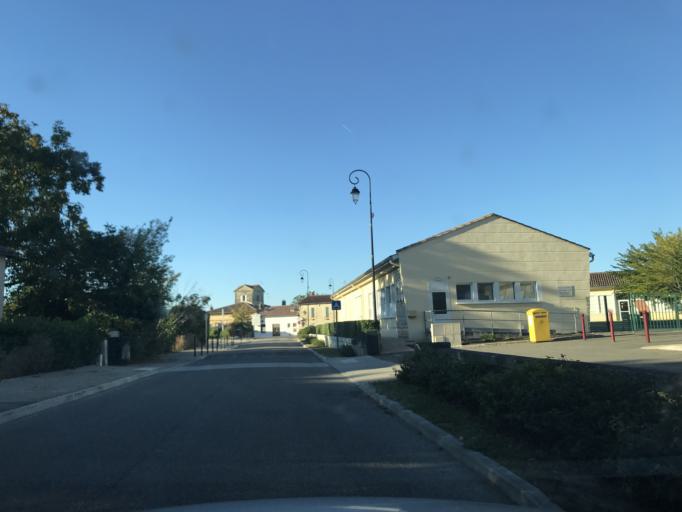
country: FR
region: Aquitaine
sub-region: Departement de la Gironde
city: Sauveterre-de-Guyenne
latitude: 44.7478
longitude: -0.0729
